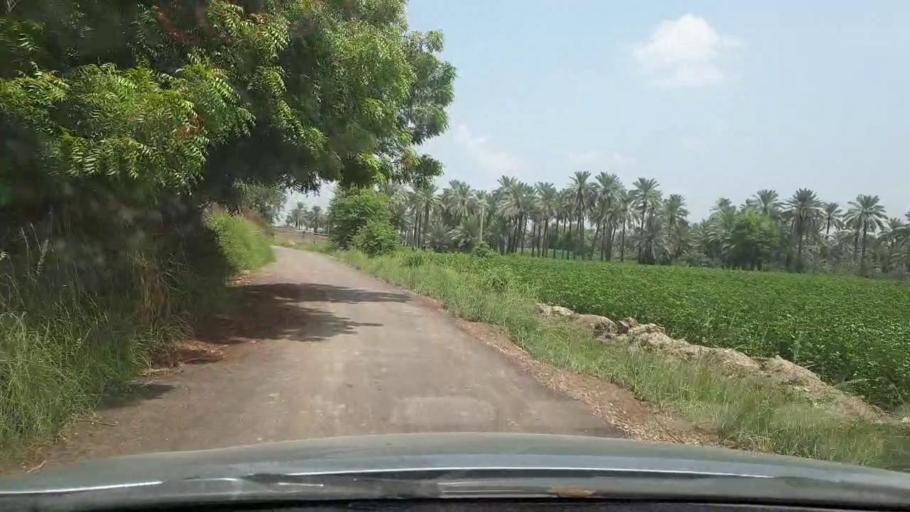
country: PK
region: Sindh
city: Khairpur
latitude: 27.4716
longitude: 68.7322
